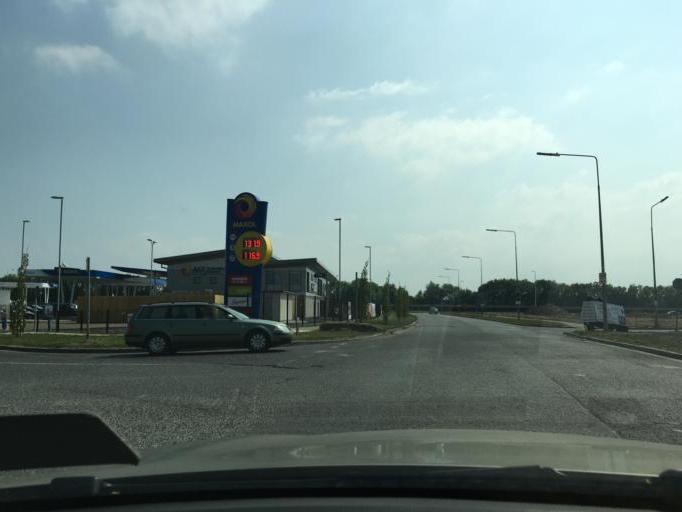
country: IE
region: Leinster
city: Hartstown
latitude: 53.4075
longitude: -6.4108
